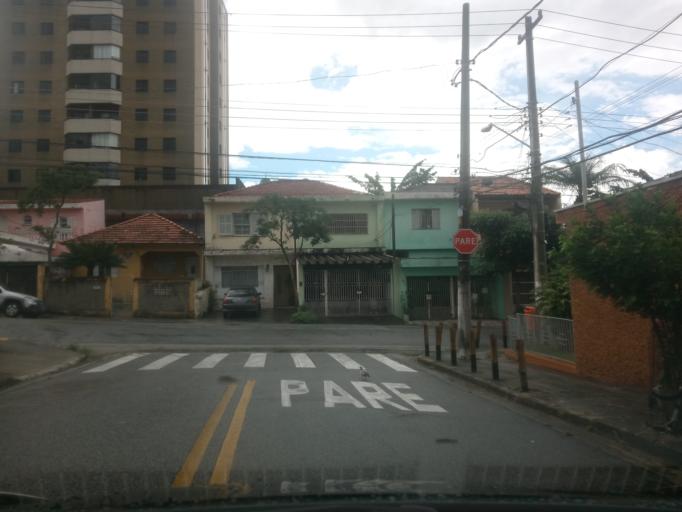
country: BR
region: Sao Paulo
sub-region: Sao Bernardo Do Campo
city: Sao Bernardo do Campo
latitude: -23.7001
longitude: -46.5584
